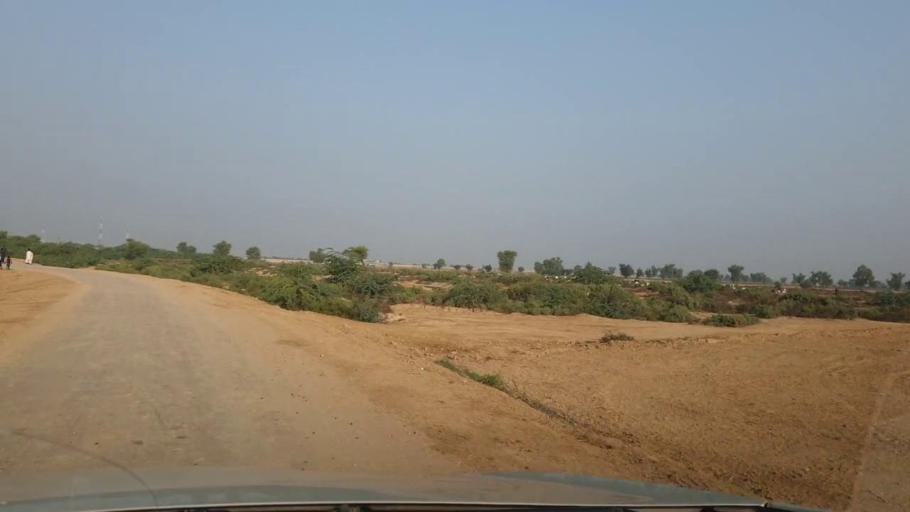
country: PK
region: Sindh
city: Sehwan
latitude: 26.3357
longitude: 67.7307
